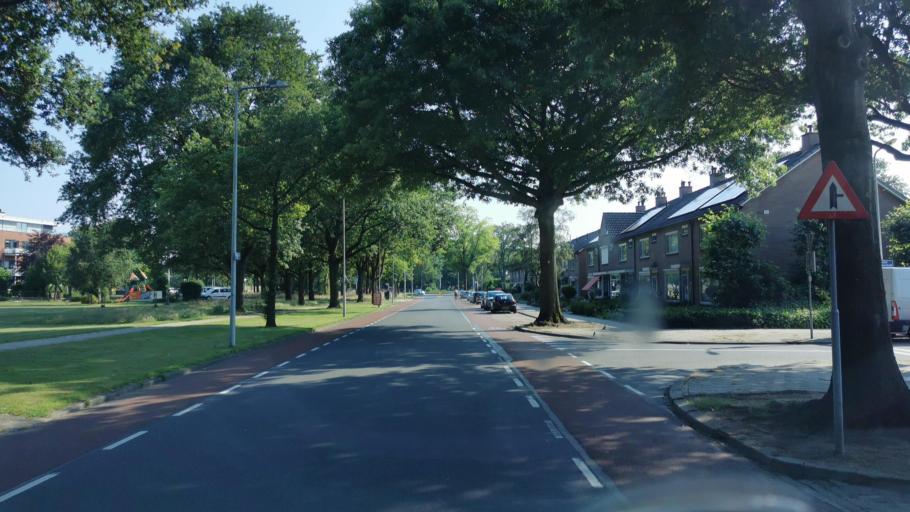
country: NL
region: Overijssel
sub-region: Gemeente Oldenzaal
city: Oldenzaal
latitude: 52.3104
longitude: 6.9094
